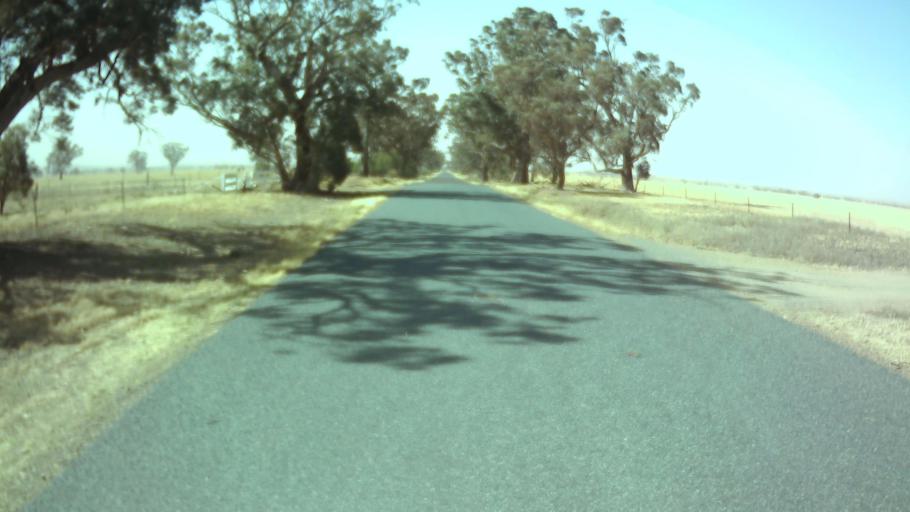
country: AU
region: New South Wales
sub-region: Weddin
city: Grenfell
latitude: -33.8928
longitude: 147.9222
